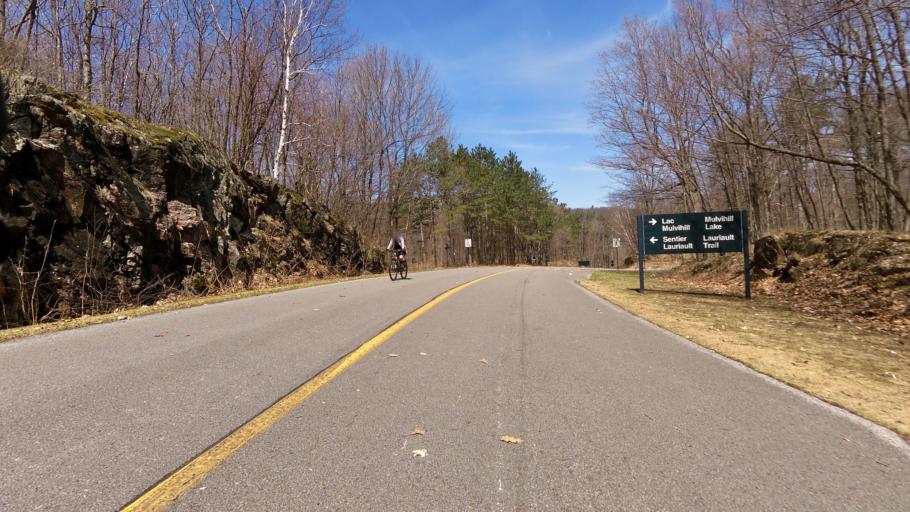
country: CA
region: Quebec
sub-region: Outaouais
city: Gatineau
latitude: 45.4835
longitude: -75.8576
